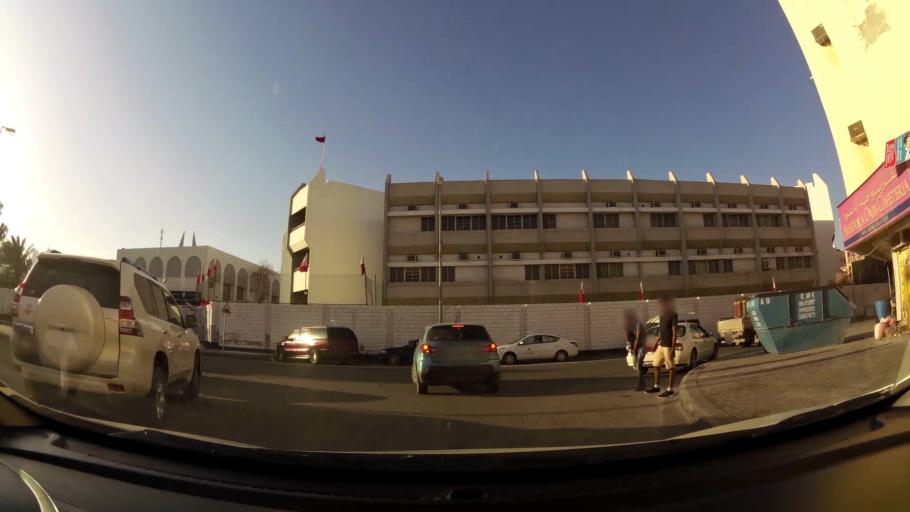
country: BH
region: Manama
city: Manama
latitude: 26.2338
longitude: 50.5906
